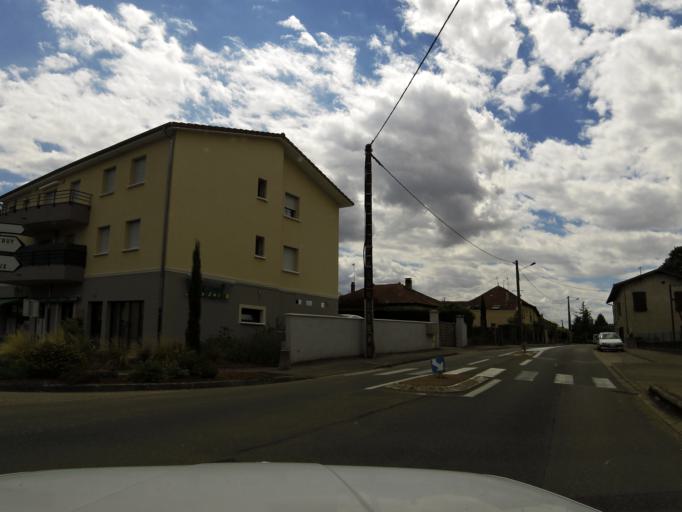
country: FR
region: Rhone-Alpes
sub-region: Departement de l'Isere
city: Saint-Romain-de-Jalionas
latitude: 45.7573
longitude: 5.2189
